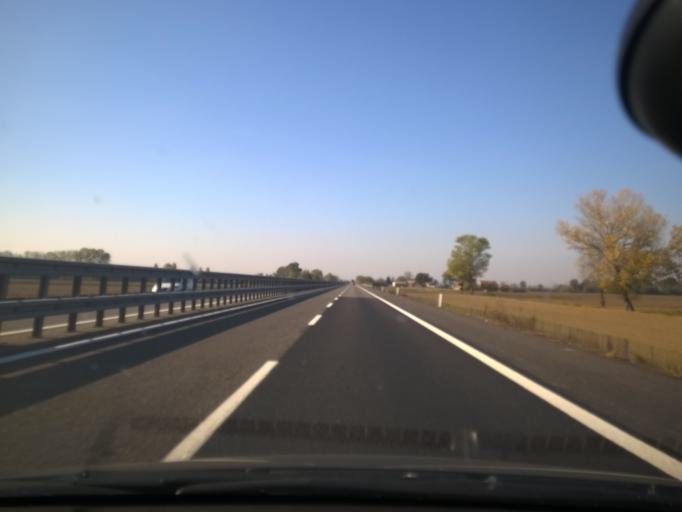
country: IT
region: Emilia-Romagna
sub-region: Provincia di Piacenza
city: Sarmato
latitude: 45.0684
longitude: 9.5105
